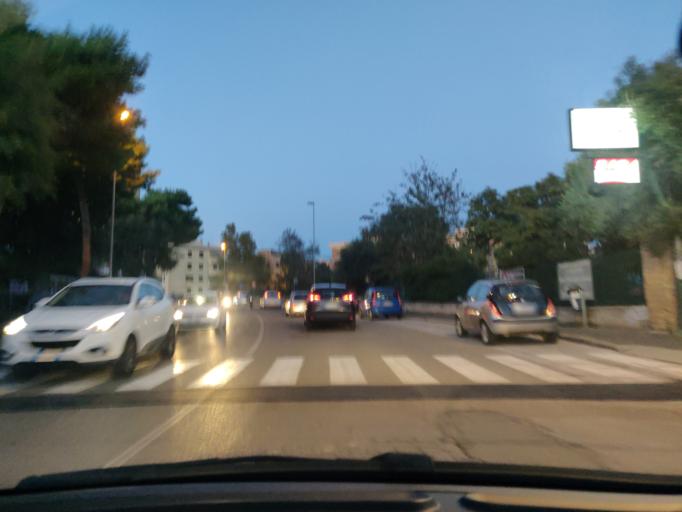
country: IT
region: Latium
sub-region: Citta metropolitana di Roma Capitale
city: Civitavecchia
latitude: 42.0872
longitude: 11.8070
